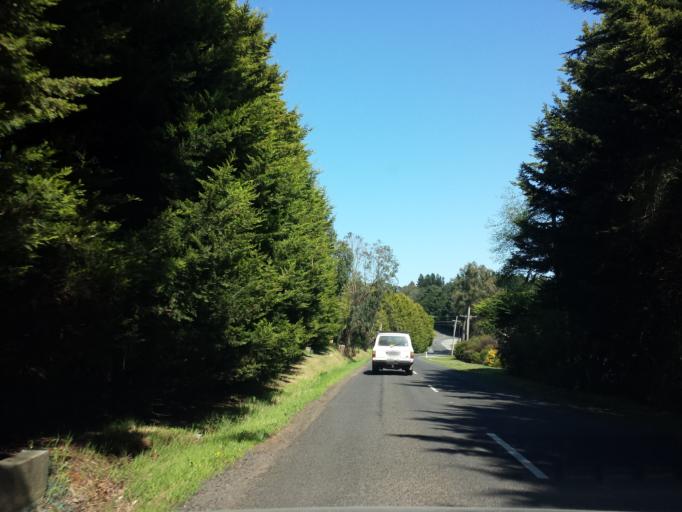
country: AU
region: Victoria
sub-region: Yarra Ranges
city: Macclesfield
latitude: -37.8152
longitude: 145.4617
